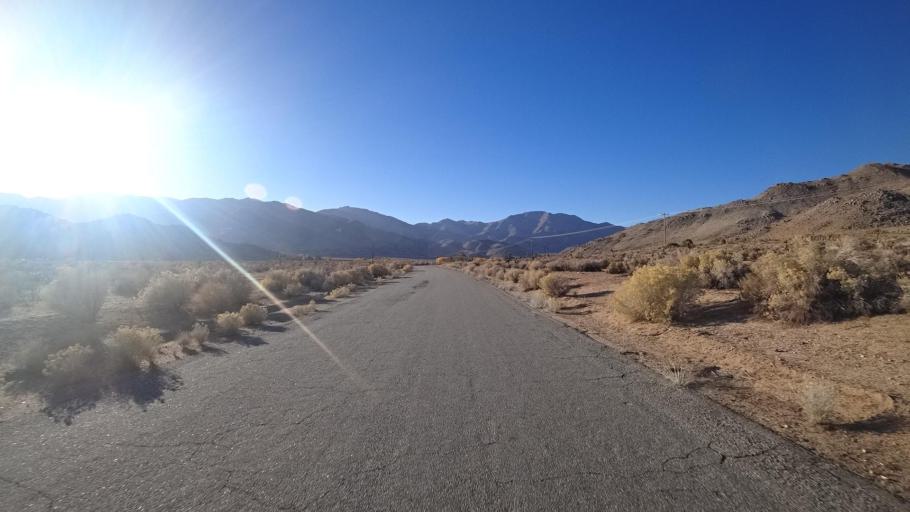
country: US
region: California
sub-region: Kern County
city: Weldon
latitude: 35.5573
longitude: -118.2254
